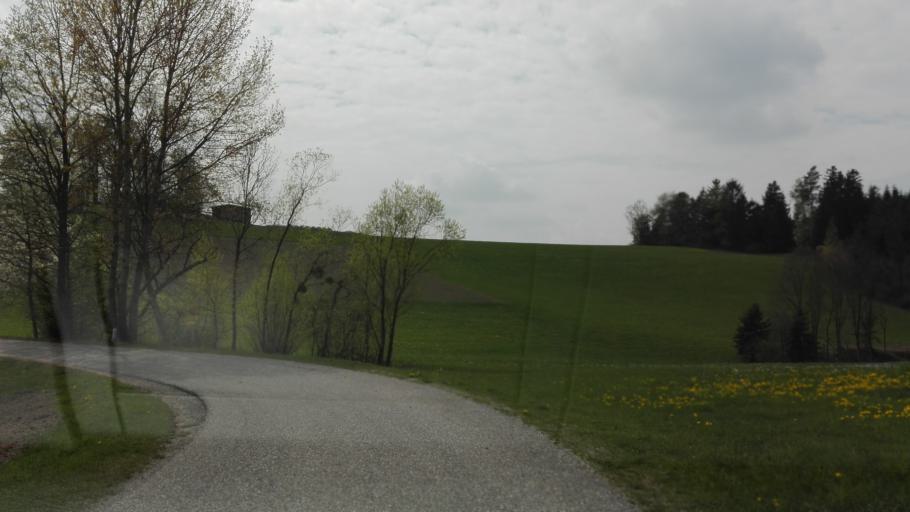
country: AT
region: Upper Austria
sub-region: Politischer Bezirk Perg
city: Perg
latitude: 48.2653
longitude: 14.6923
